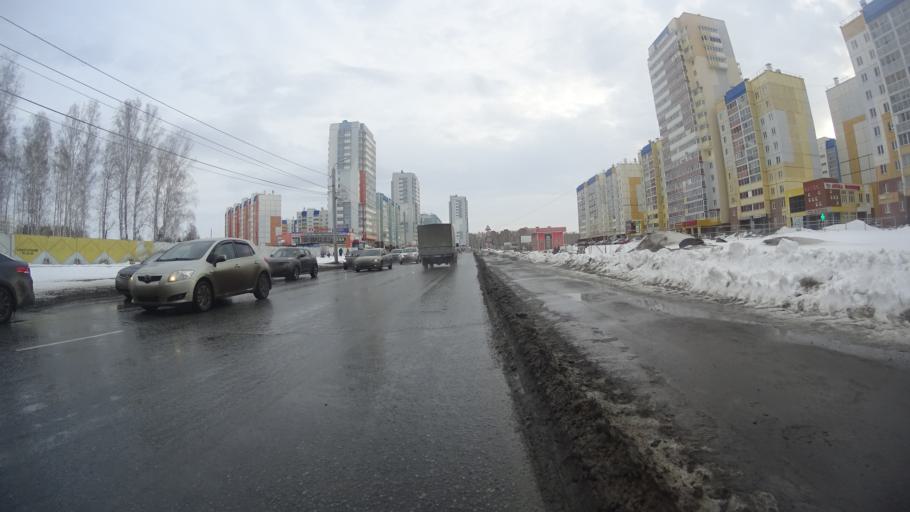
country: RU
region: Chelyabinsk
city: Roshchino
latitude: 55.2054
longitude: 61.2843
